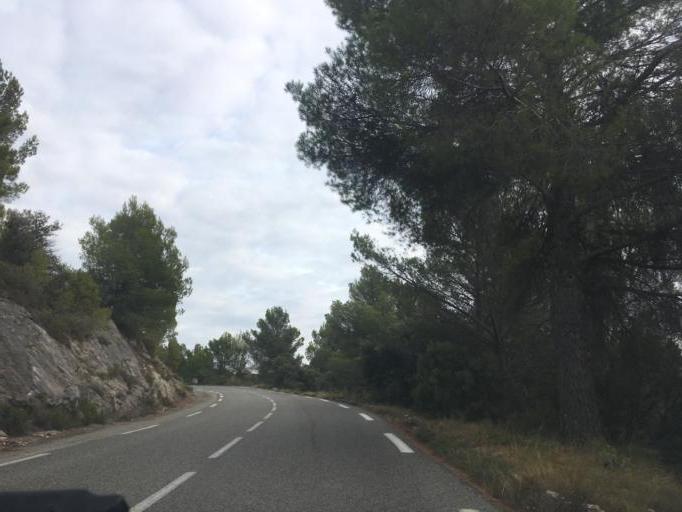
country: FR
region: Provence-Alpes-Cote d'Azur
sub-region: Departement du Var
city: Villecroze
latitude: 43.5884
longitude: 6.2732
